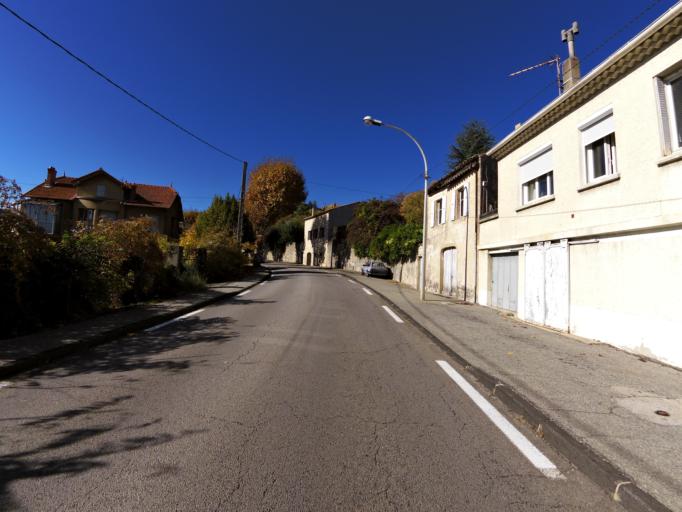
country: FR
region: Rhone-Alpes
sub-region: Departement de l'Ardeche
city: Privas
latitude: 44.7324
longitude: 4.5862
